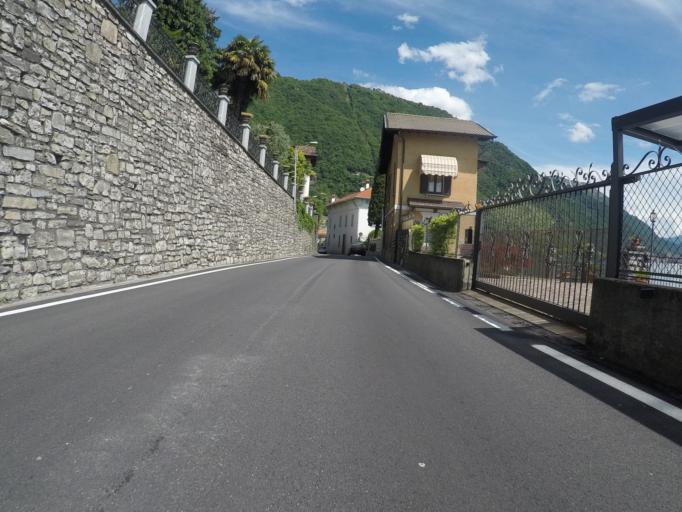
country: IT
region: Lombardy
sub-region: Provincia di Como
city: Argegno
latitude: 45.9402
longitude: 9.1282
